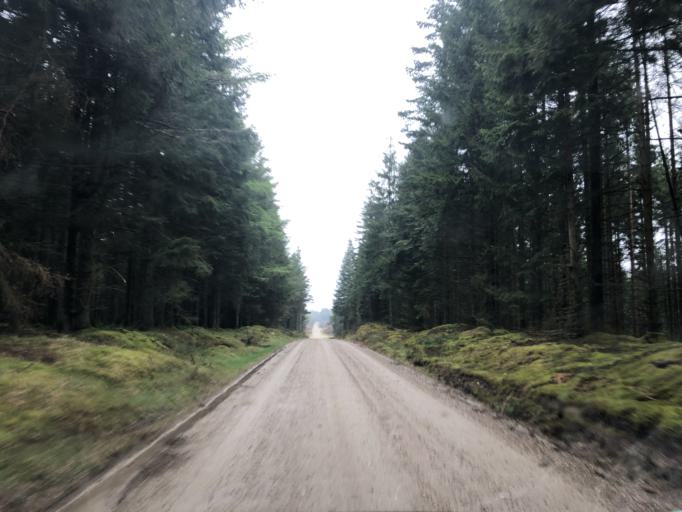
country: DK
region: Central Jutland
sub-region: Lemvig Kommune
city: Lemvig
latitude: 56.4704
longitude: 8.3857
